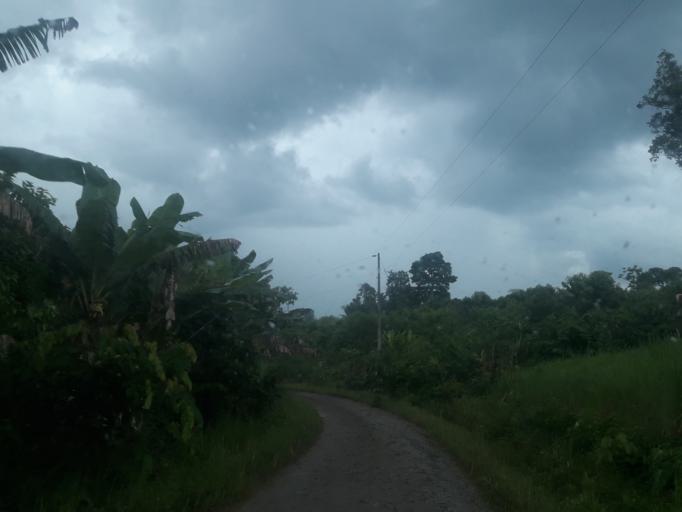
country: EC
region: Napo
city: Tena
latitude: -1.0923
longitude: -77.7019
